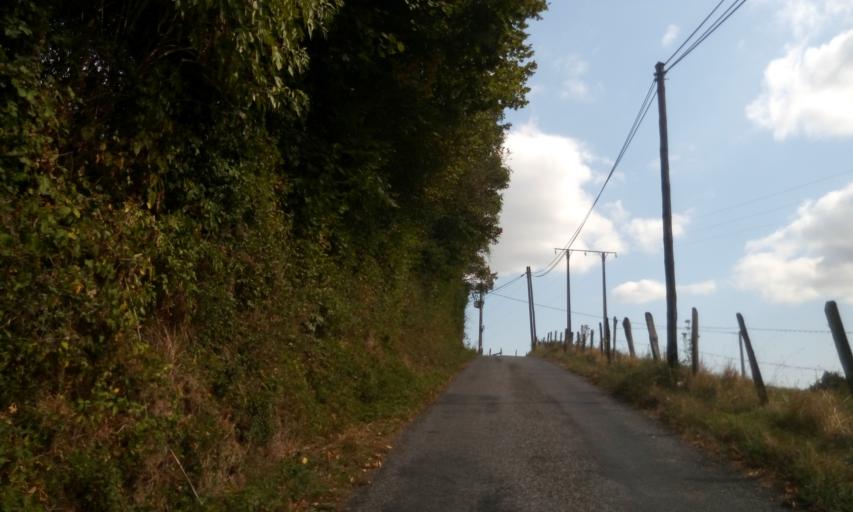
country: FR
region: Rhone-Alpes
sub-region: Departement du Rhone
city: Grandris
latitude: 46.0059
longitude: 4.4665
